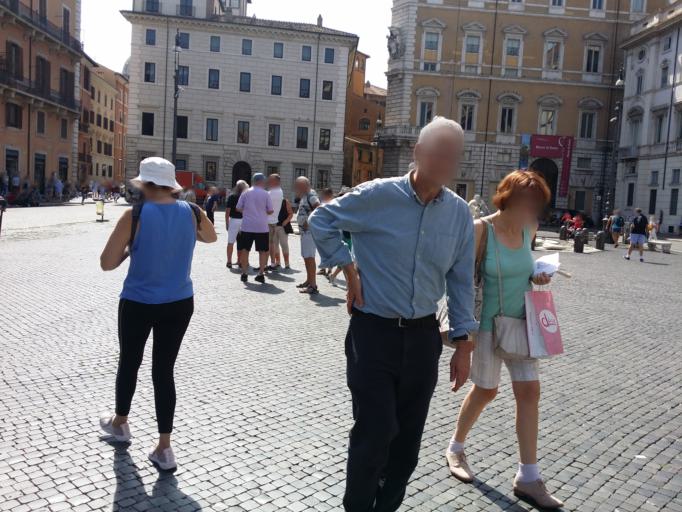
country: VA
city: Vatican City
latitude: 41.8985
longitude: 12.4732
